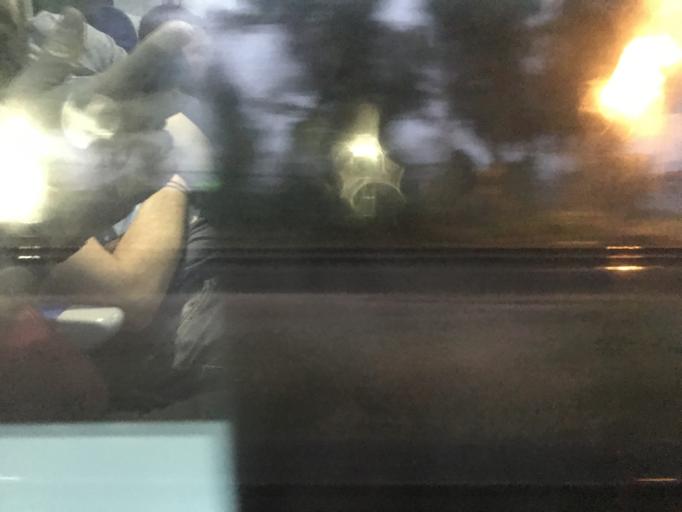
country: TR
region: Kocaeli
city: Korfez
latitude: 40.7726
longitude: 29.7313
